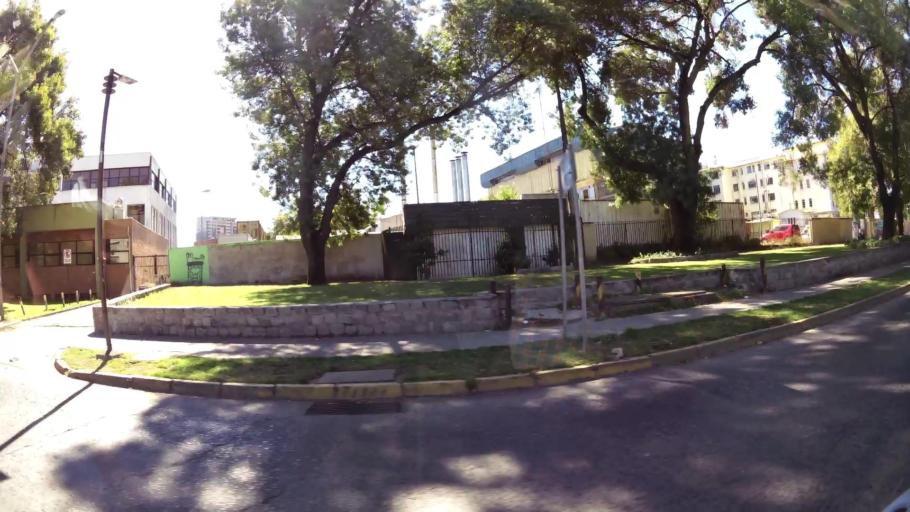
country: CL
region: Biobio
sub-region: Provincia de Concepcion
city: Concepcion
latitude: -36.8262
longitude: -73.0376
